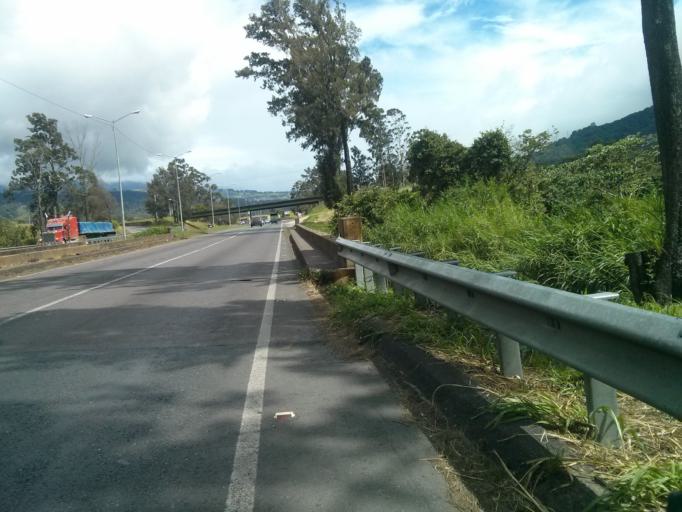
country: CR
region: Cartago
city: Tres Rios
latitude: 9.9018
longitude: -83.9907
